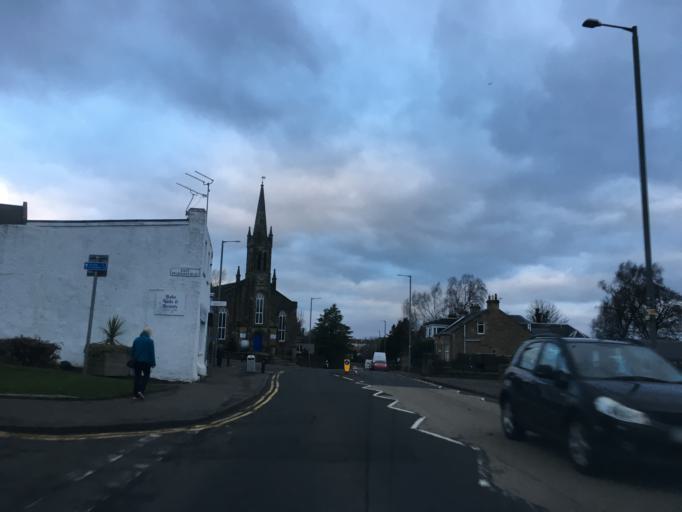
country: GB
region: Scotland
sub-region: Stirling
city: Bannockburn
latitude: 56.0904
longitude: -3.9121
